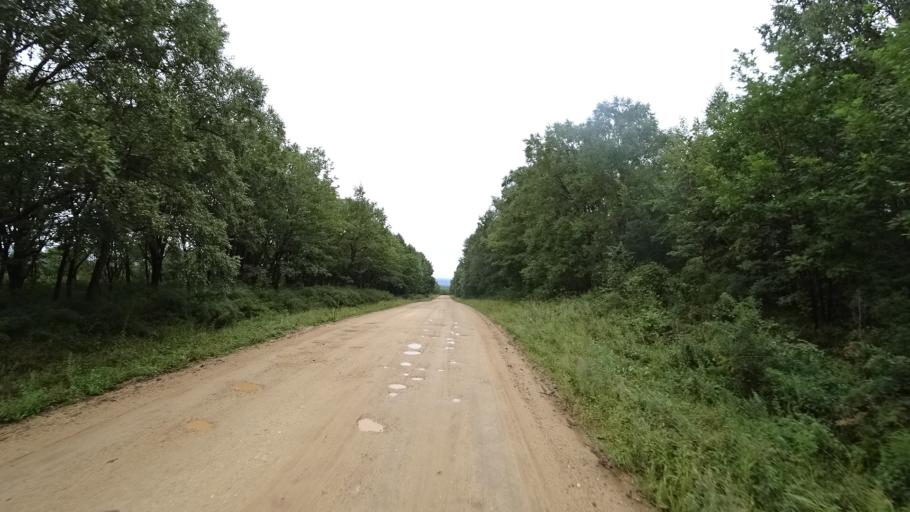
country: RU
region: Primorskiy
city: Ivanovka
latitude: 44.0473
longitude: 132.5456
